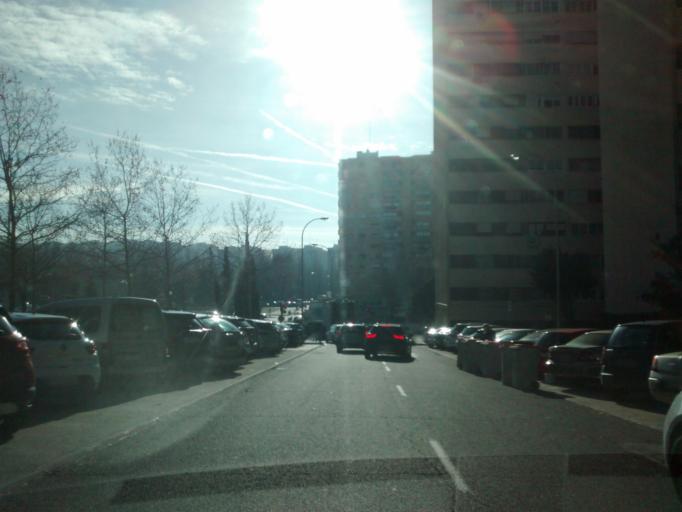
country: ES
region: Madrid
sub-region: Provincia de Madrid
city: Tetuan de las Victorias
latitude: 40.4812
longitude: -3.7138
